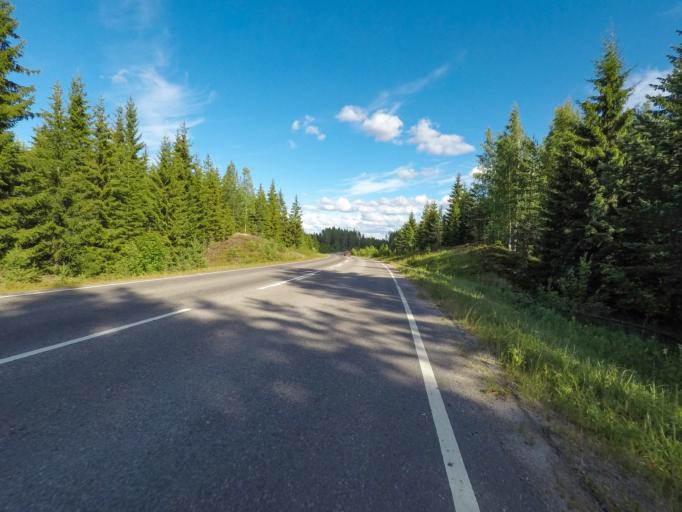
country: FI
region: South Karelia
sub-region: Lappeenranta
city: Joutseno
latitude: 61.1468
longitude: 28.6197
